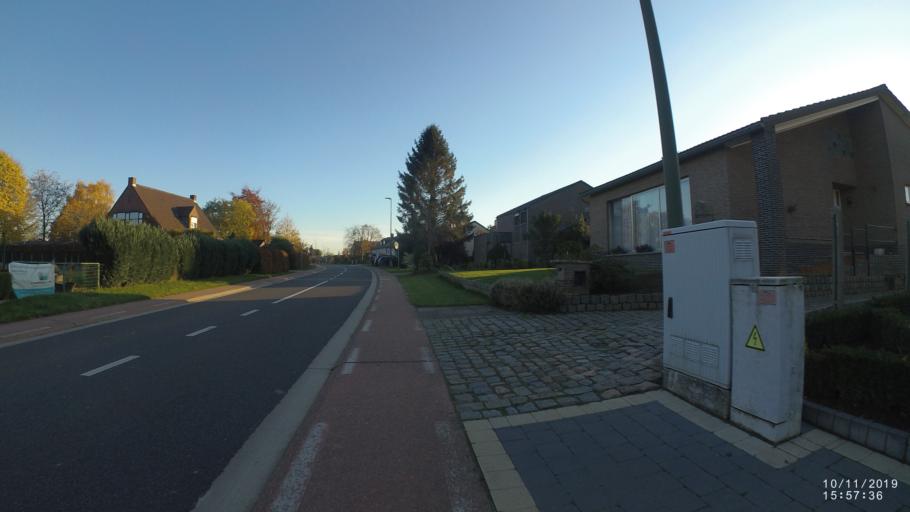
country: BE
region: Flanders
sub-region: Provincie Vlaams-Brabant
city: Lubbeek
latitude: 50.9029
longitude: 4.8864
